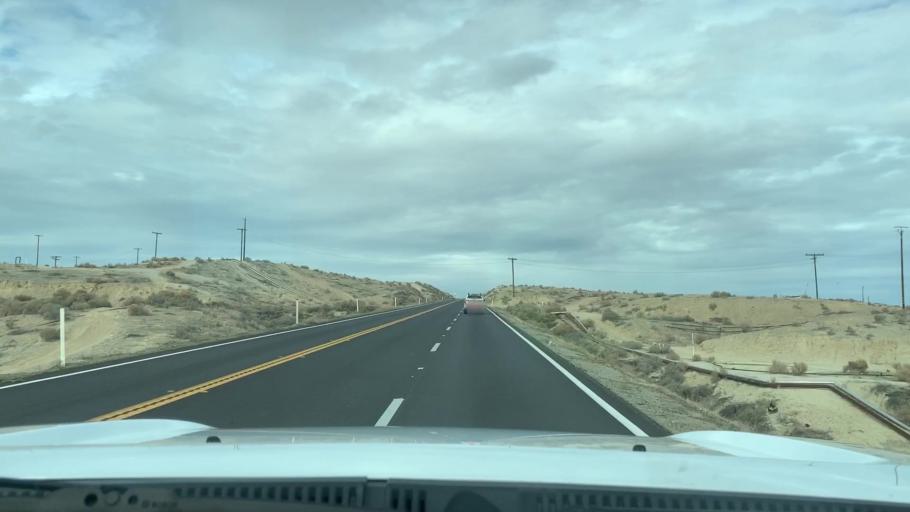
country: US
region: California
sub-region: Kern County
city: Maricopa
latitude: 35.1001
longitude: -119.4149
